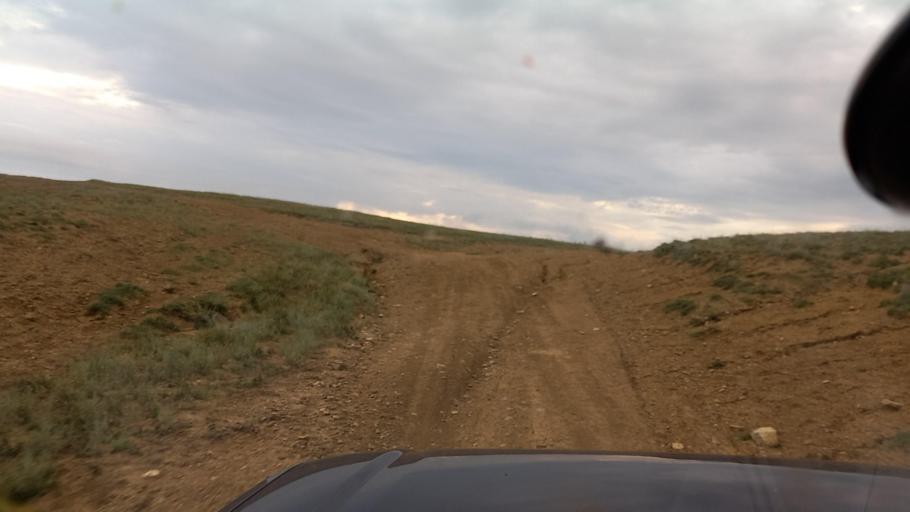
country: RU
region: Krasnodarskiy
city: Taman'
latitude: 45.2016
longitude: 36.7908
